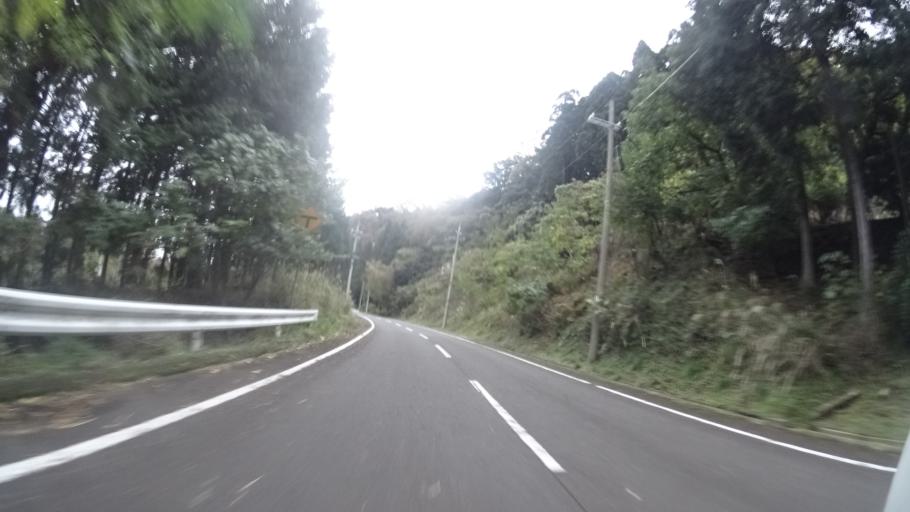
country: JP
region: Kyoto
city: Maizuru
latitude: 35.5657
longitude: 135.4587
